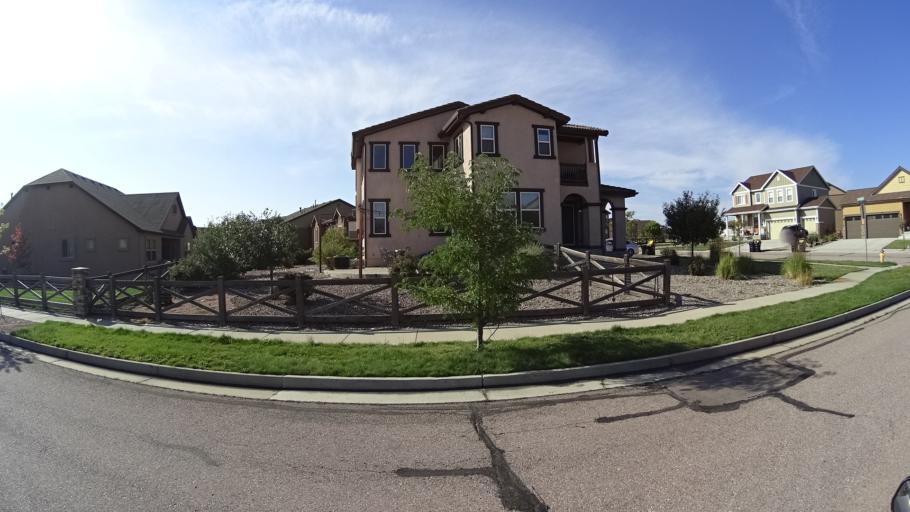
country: US
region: Colorado
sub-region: El Paso County
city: Black Forest
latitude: 38.9370
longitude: -104.6778
